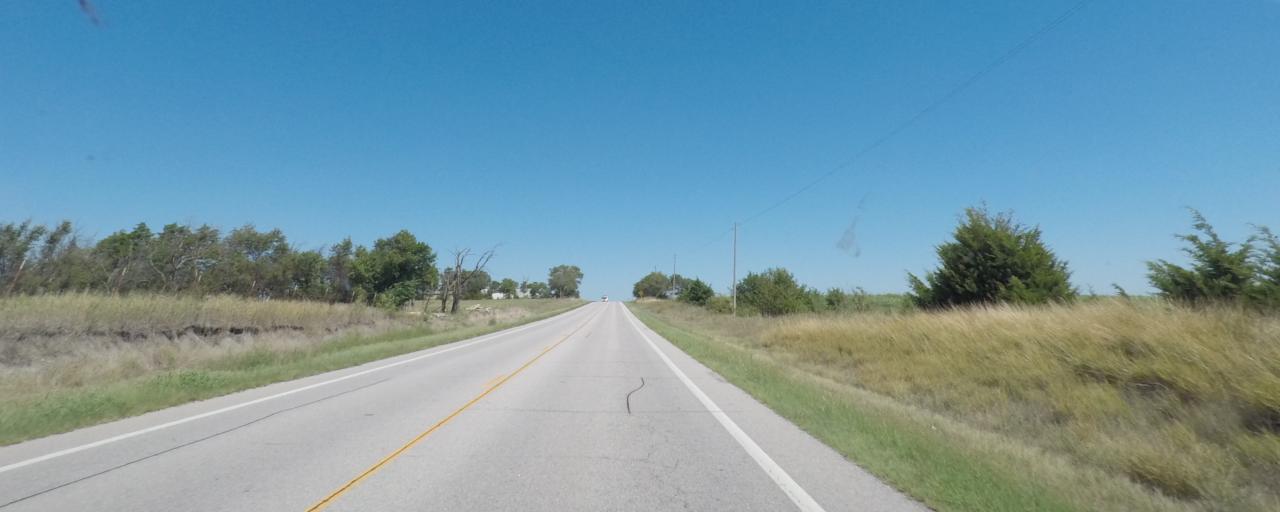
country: US
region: Kansas
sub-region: Sumner County
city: Wellington
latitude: 37.2281
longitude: -97.4025
